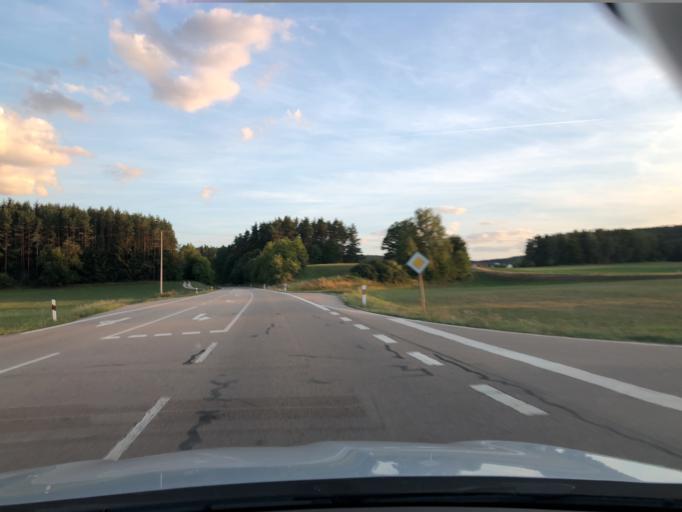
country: DE
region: Bavaria
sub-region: Upper Palatinate
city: Illschwang
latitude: 49.4812
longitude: 11.7046
